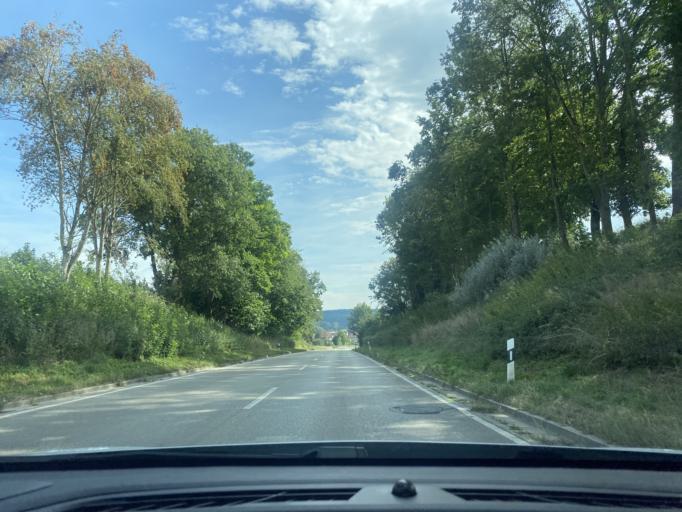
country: DE
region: Bavaria
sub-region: Upper Bavaria
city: Zolling
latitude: 48.4586
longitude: 11.7683
